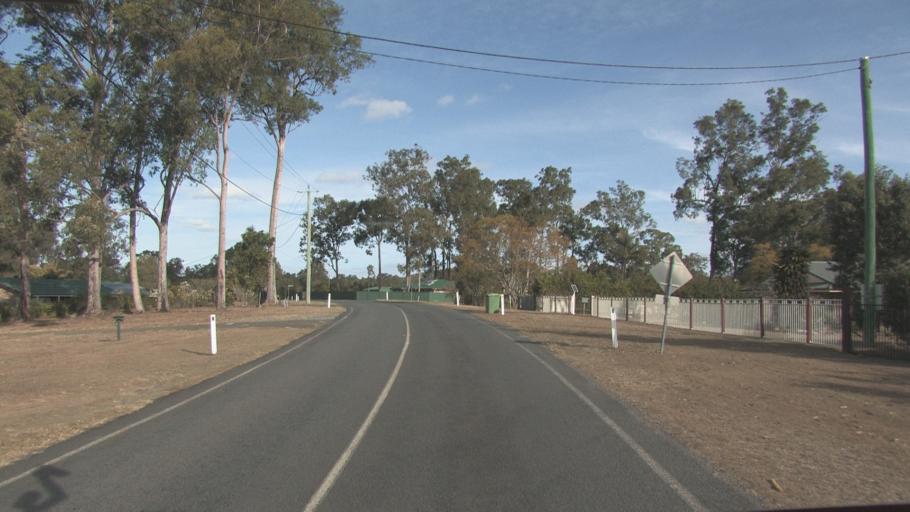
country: AU
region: Queensland
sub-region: Logan
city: Cedar Vale
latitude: -27.8685
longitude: 153.0036
